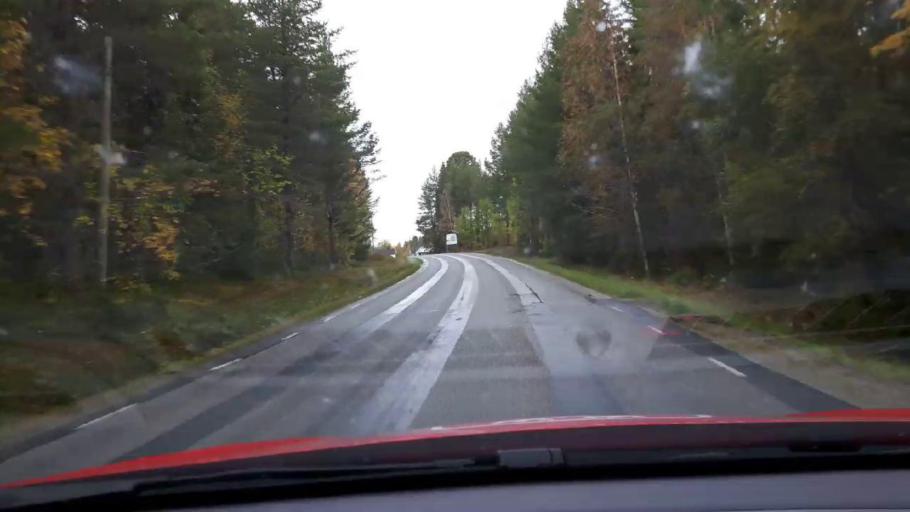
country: SE
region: Jaemtland
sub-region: Bergs Kommun
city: Hoverberg
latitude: 62.8786
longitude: 14.3660
